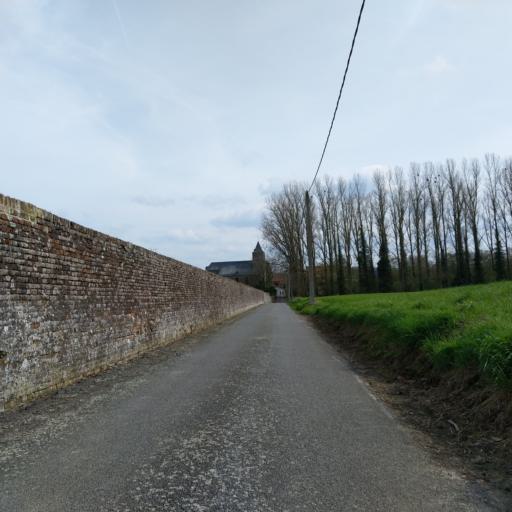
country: BE
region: Wallonia
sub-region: Province du Hainaut
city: Jurbise
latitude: 50.5386
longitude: 3.9558
